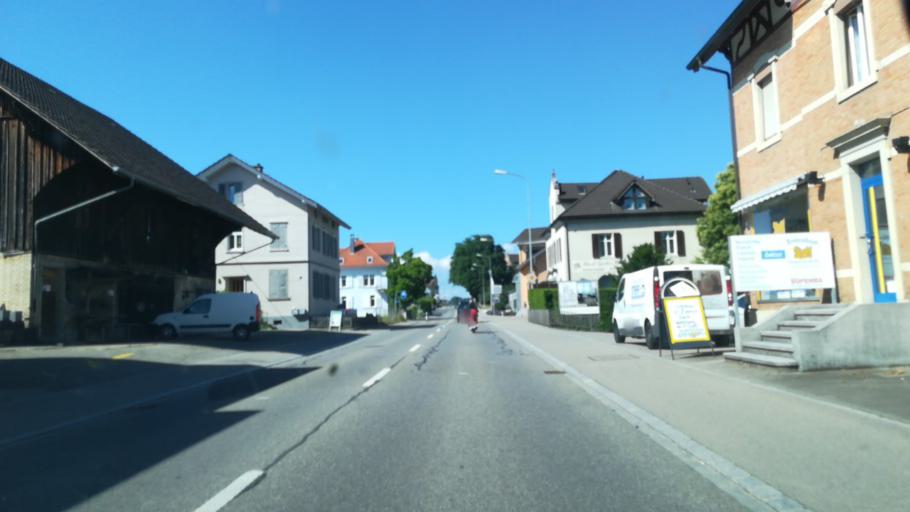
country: CH
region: Thurgau
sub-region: Weinfelden District
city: Berg
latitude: 47.5804
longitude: 9.1674
